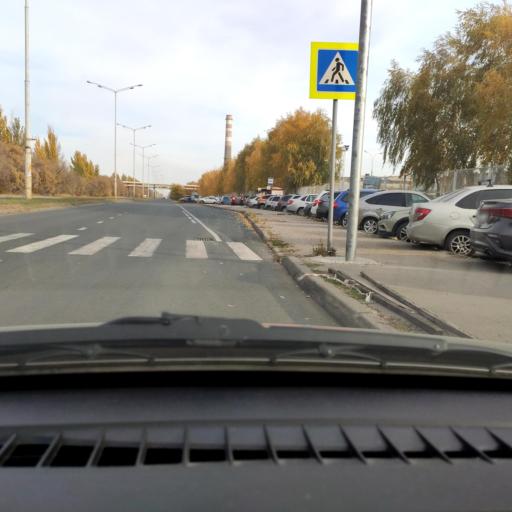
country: RU
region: Samara
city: Tol'yatti
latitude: 53.5707
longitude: 49.2440
